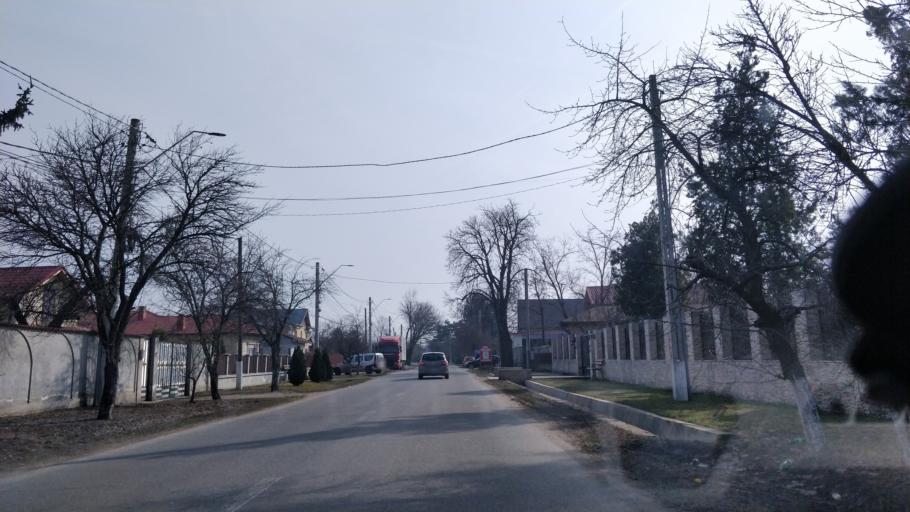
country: RO
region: Giurgiu
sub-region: Comuna Ulmi
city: Ulmi
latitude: 44.4658
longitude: 25.7734
